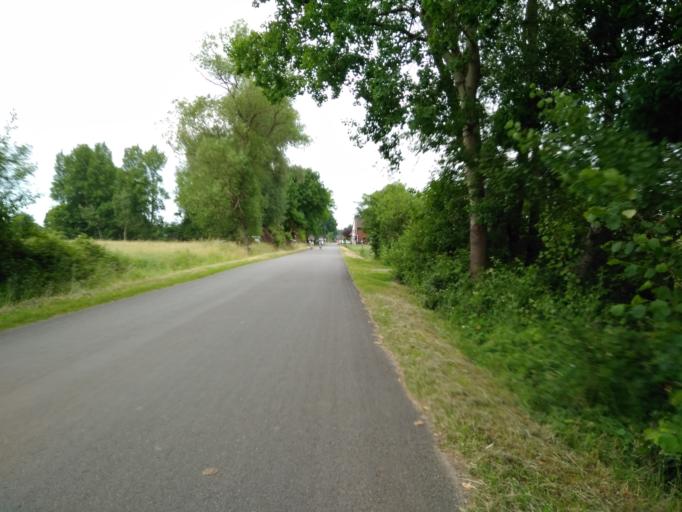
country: DE
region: North Rhine-Westphalia
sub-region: Regierungsbezirk Dusseldorf
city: Schermbeck
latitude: 51.6594
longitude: 6.8574
